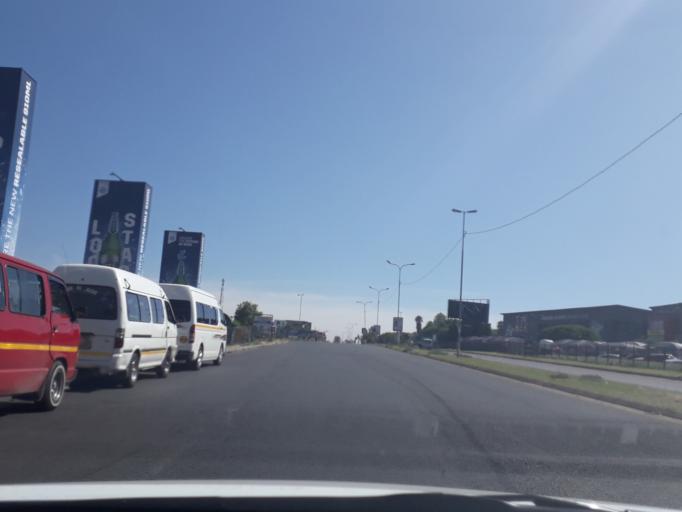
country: ZA
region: Gauteng
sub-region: City of Johannesburg Metropolitan Municipality
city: Diepsloot
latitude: -26.0596
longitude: 28.0219
